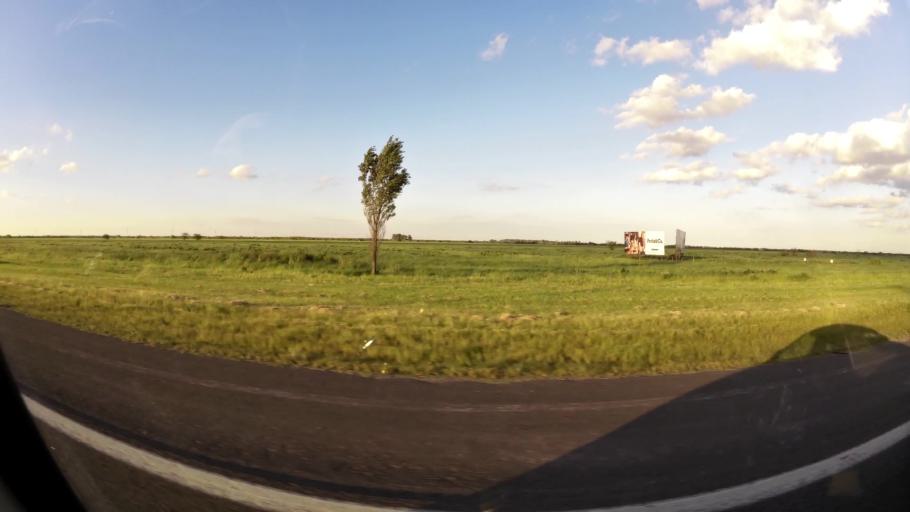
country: AR
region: Buenos Aires
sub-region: Partido de La Plata
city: La Plata
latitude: -34.8516
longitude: -58.0412
